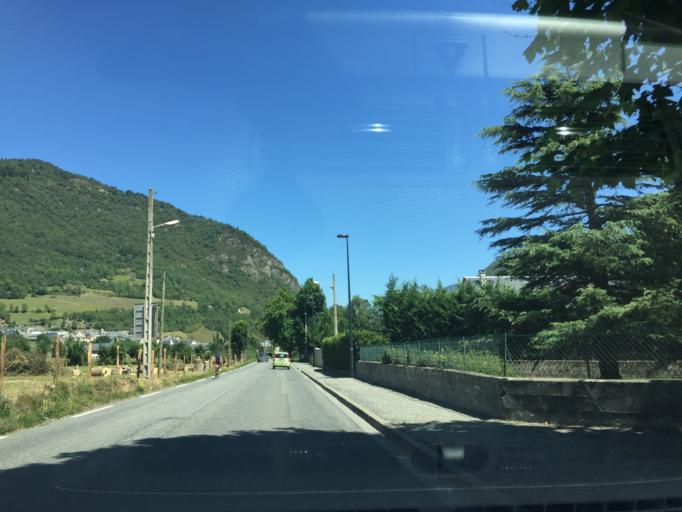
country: FR
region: Midi-Pyrenees
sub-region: Departement des Hautes-Pyrenees
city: Saint-Lary-Soulan
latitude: 42.8660
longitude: 0.3393
